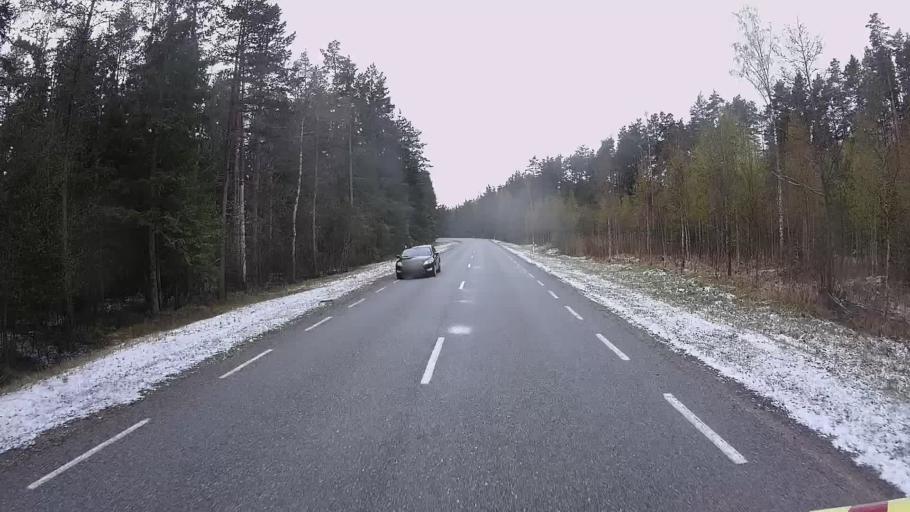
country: EE
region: Hiiumaa
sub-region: Kaerdla linn
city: Kardla
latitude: 59.0310
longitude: 22.6751
